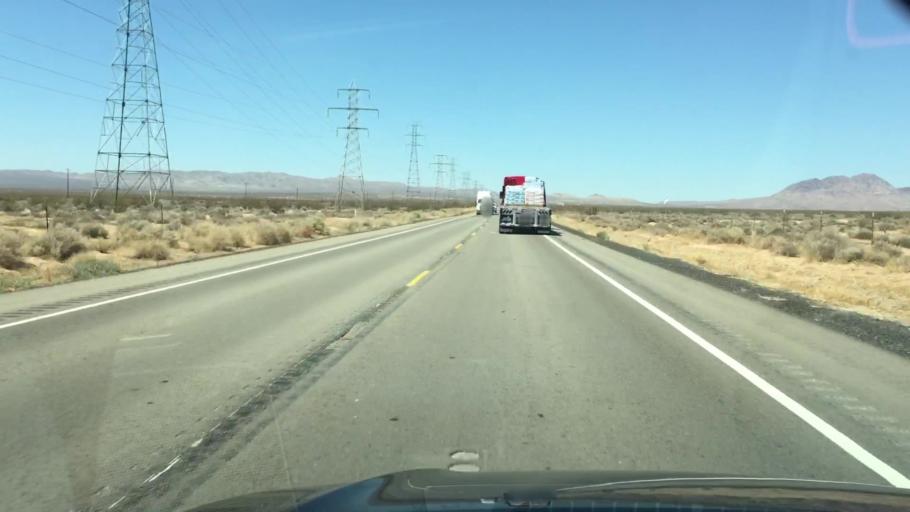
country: US
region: California
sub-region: Kern County
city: Boron
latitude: 35.2178
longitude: -117.6044
